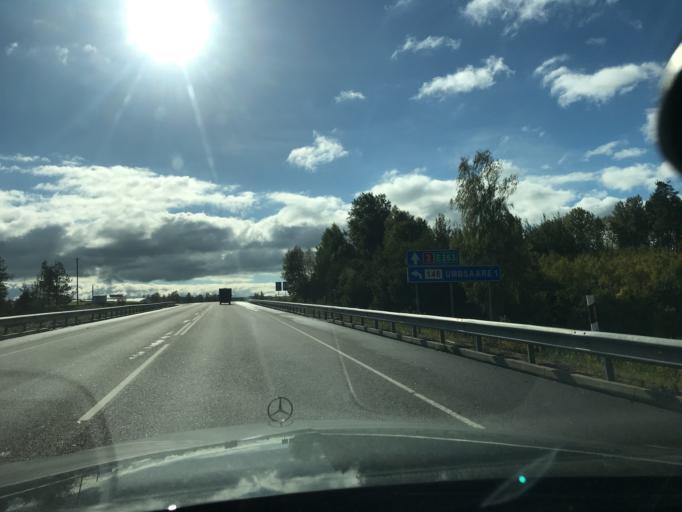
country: EE
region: Vorumaa
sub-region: Voru linn
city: Voru
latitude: 57.8193
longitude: 27.0643
